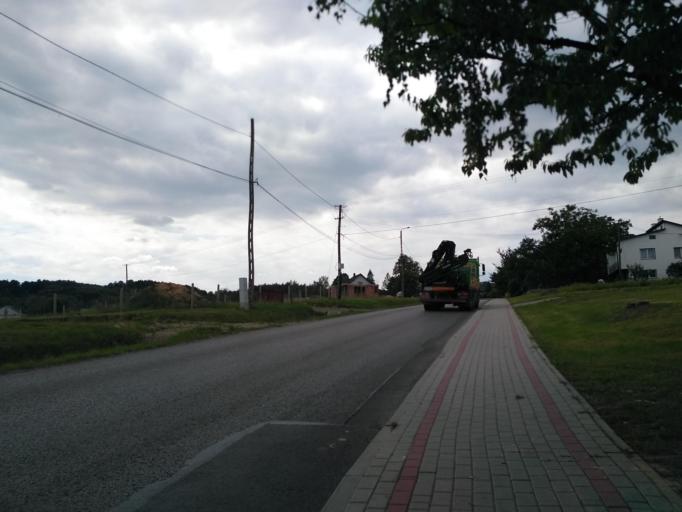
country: PL
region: Subcarpathian Voivodeship
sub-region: Powiat rzeszowski
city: Lecka
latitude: 49.8940
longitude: 22.0073
